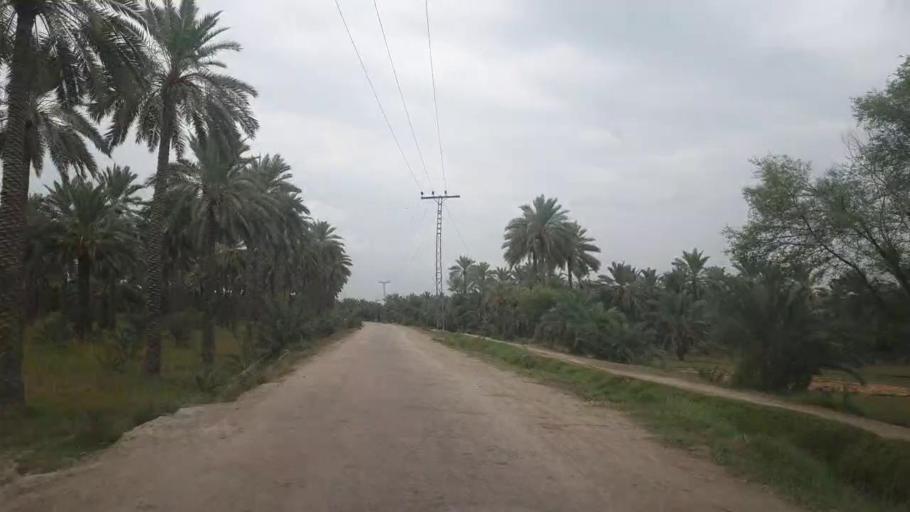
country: PK
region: Sindh
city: Khairpur
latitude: 27.5708
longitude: 68.7037
